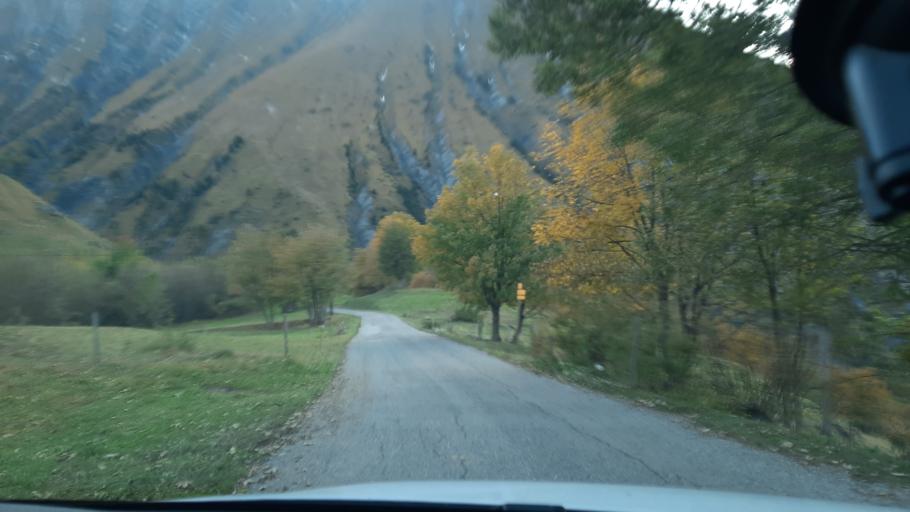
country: FR
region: Rhone-Alpes
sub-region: Departement de la Savoie
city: Villargondran
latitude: 45.1841
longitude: 6.3200
